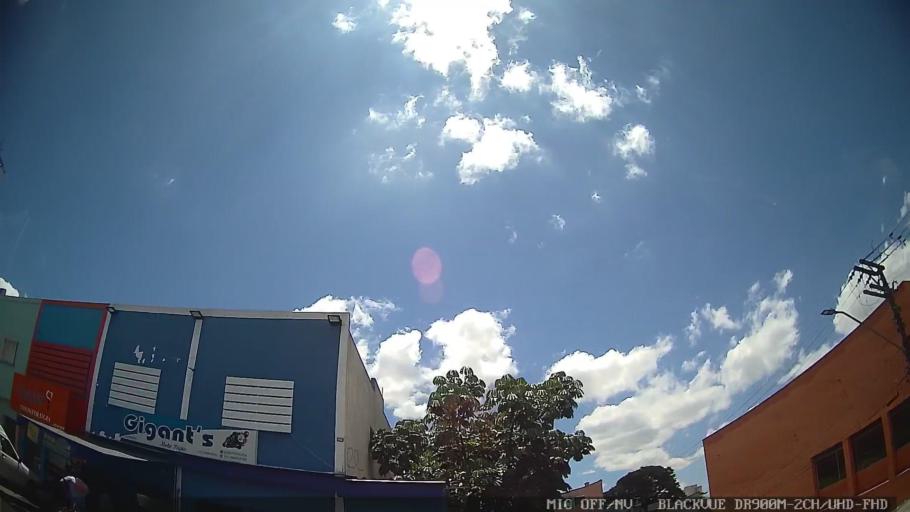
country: BR
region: Sao Paulo
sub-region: Diadema
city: Diadema
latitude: -23.6477
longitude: -46.6606
